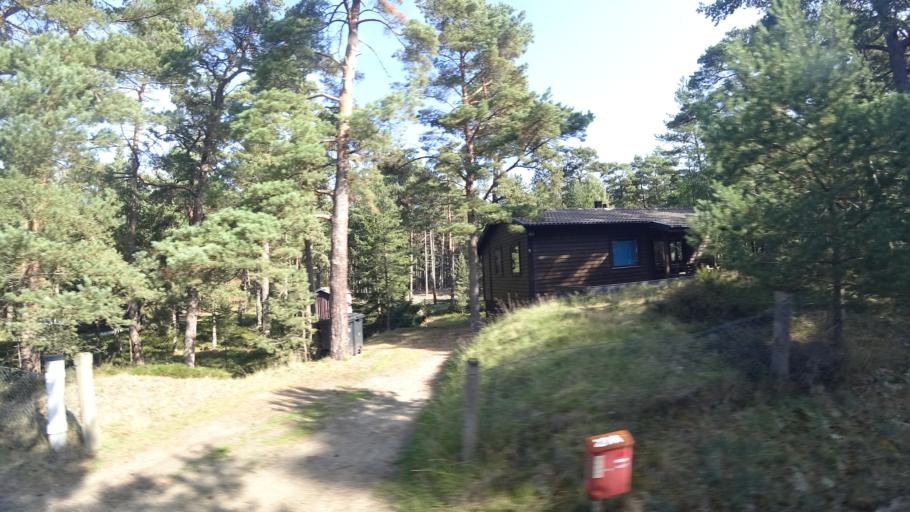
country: SE
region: Skane
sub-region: Kristianstads Kommun
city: Ahus
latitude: 55.9162
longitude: 14.3097
